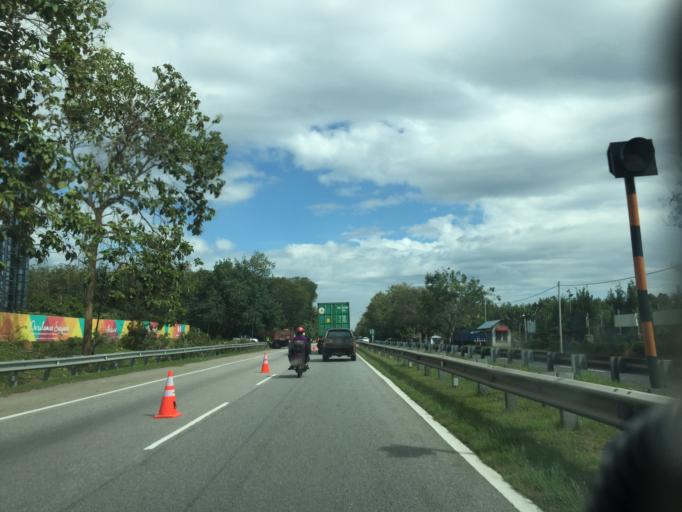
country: MY
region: Kedah
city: Jitra
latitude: 6.3455
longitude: 100.4208
